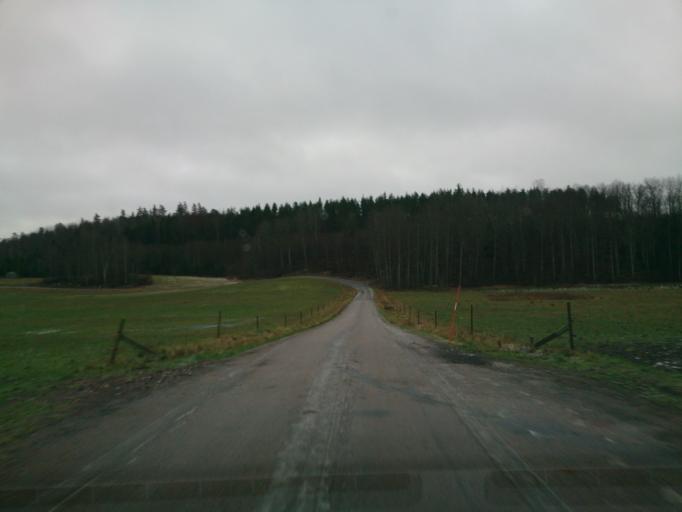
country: SE
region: OEstergoetland
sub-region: Atvidabergs Kommun
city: Atvidaberg
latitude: 58.2761
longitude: 16.1985
